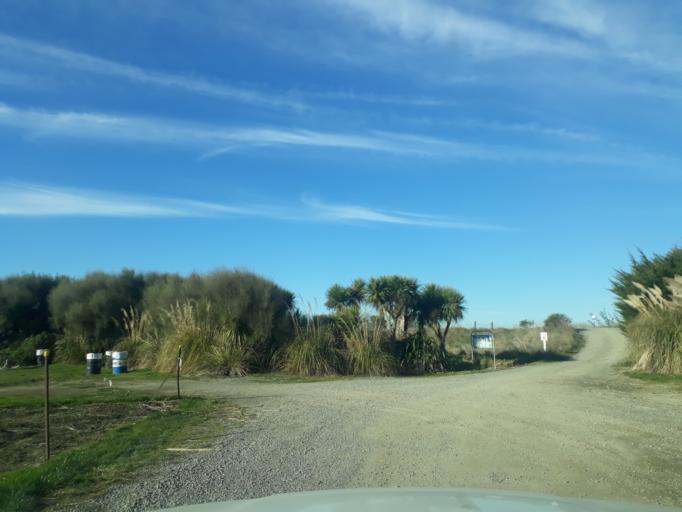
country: NZ
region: Canterbury
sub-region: Timaru District
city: Timaru
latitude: -44.2764
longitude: 171.3515
